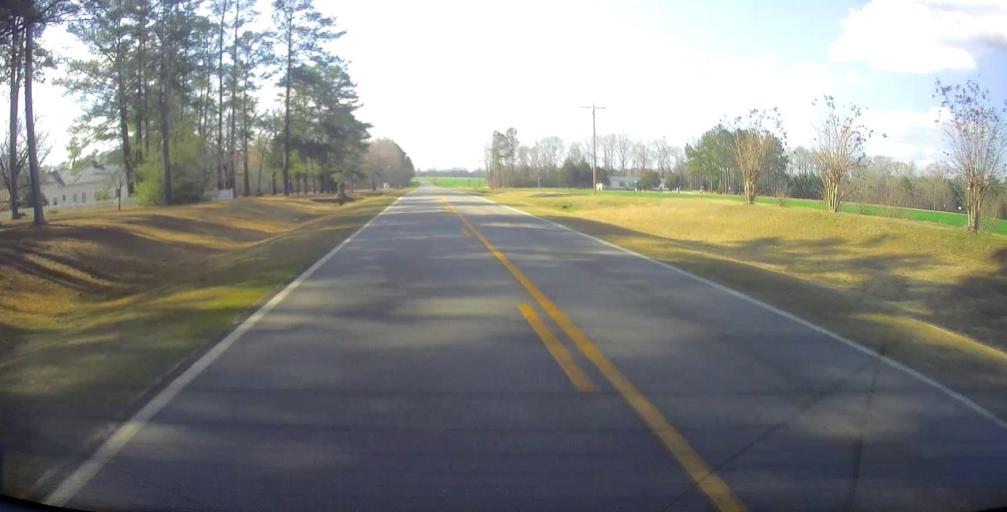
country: US
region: Georgia
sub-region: Wilkinson County
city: Irwinton
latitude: 32.6294
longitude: -83.0985
